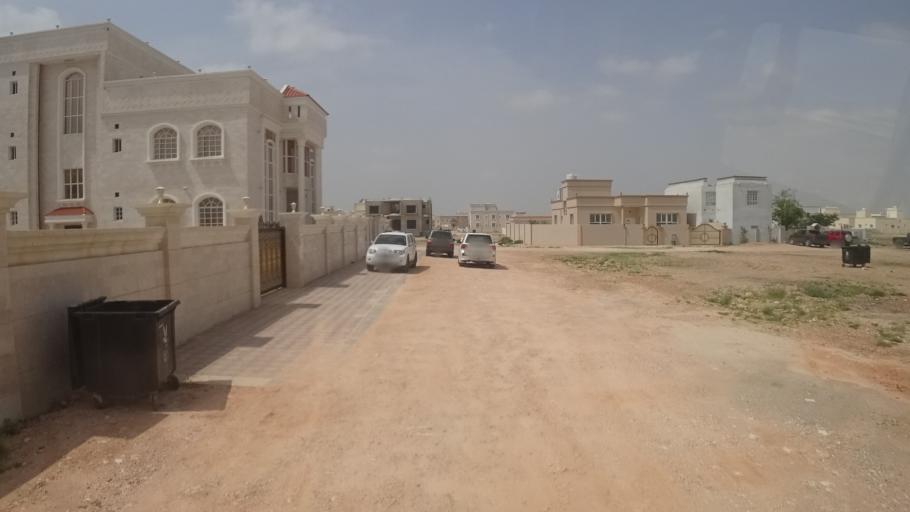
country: OM
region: Zufar
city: Salalah
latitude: 17.1025
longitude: 54.2138
